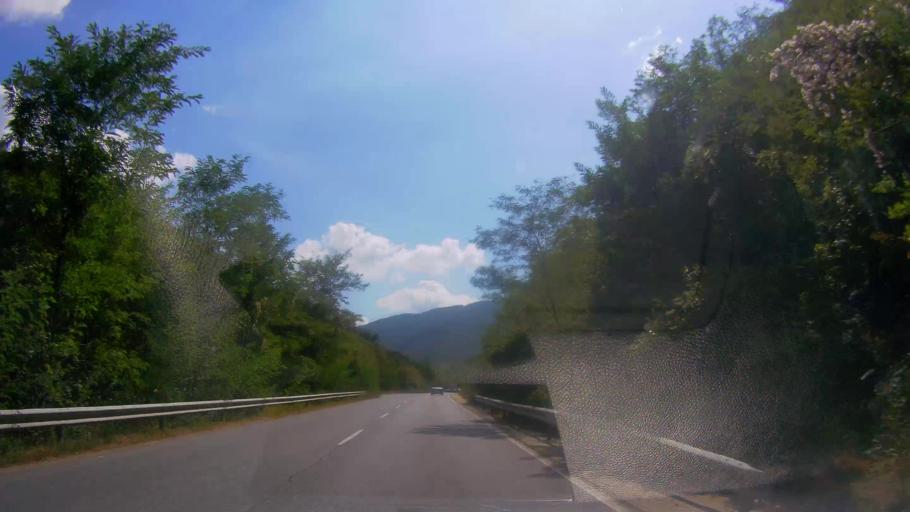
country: BG
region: Stara Zagora
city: Gurkovo
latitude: 42.7232
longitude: 25.7136
